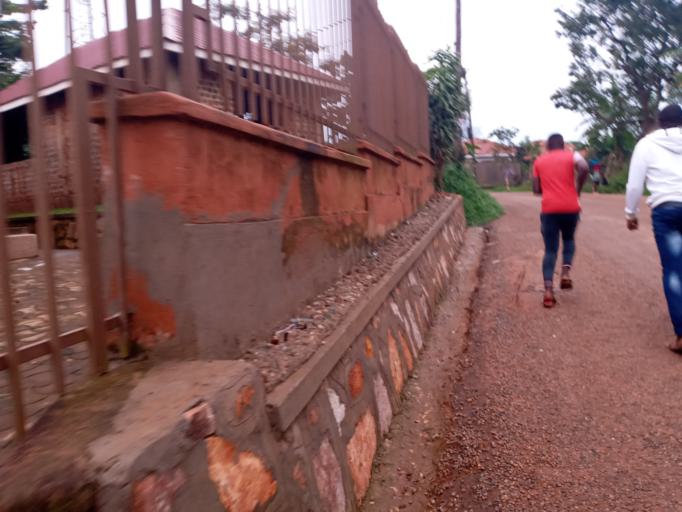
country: UG
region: Central Region
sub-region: Wakiso District
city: Bweyogerere
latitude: 0.3336
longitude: 32.6719
